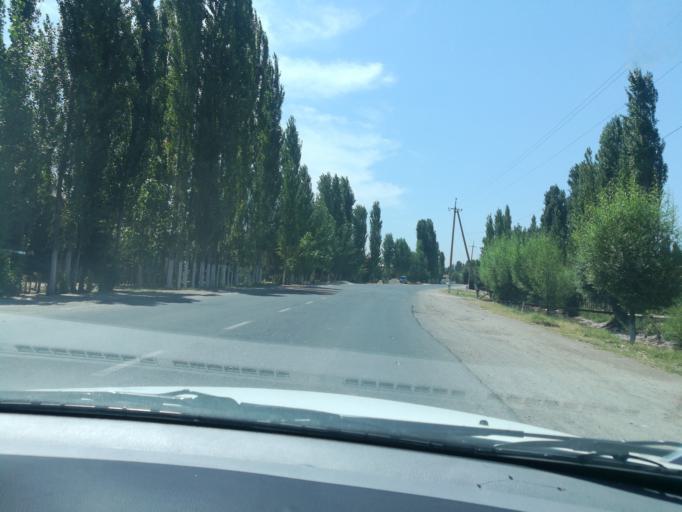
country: UZ
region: Namangan
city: Uchqurghon Shahri
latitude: 41.0755
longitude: 72.0519
